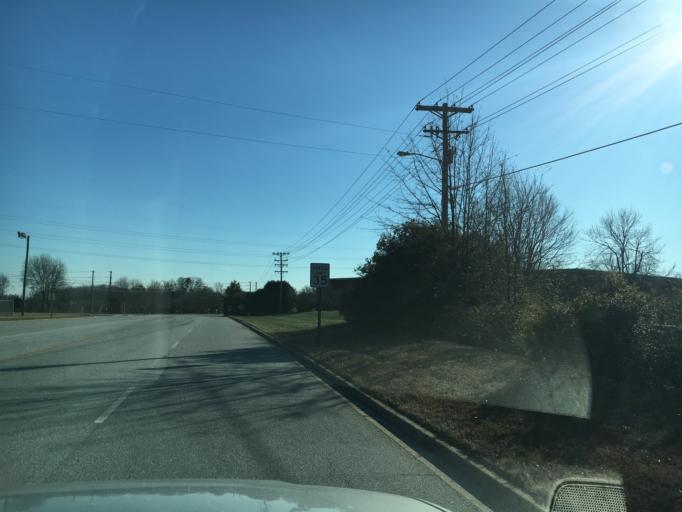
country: US
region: South Carolina
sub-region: Greenville County
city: Mauldin
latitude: 34.8101
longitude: -82.2764
